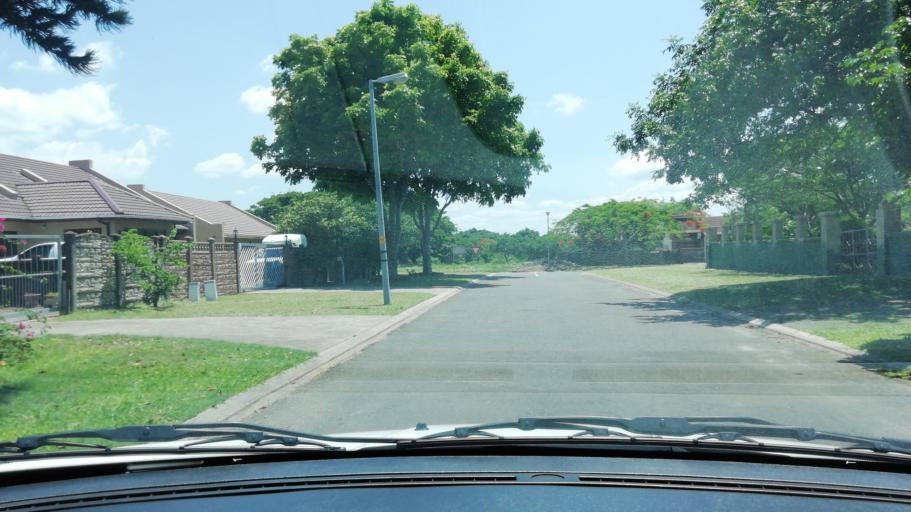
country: ZA
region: KwaZulu-Natal
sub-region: uThungulu District Municipality
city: Richards Bay
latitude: -28.7363
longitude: 32.0463
